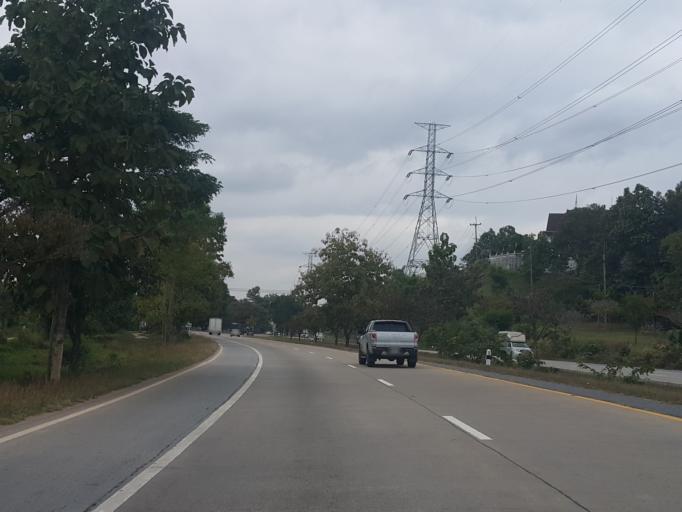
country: TH
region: Lamphun
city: Mae Tha
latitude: 18.4621
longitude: 99.1635
